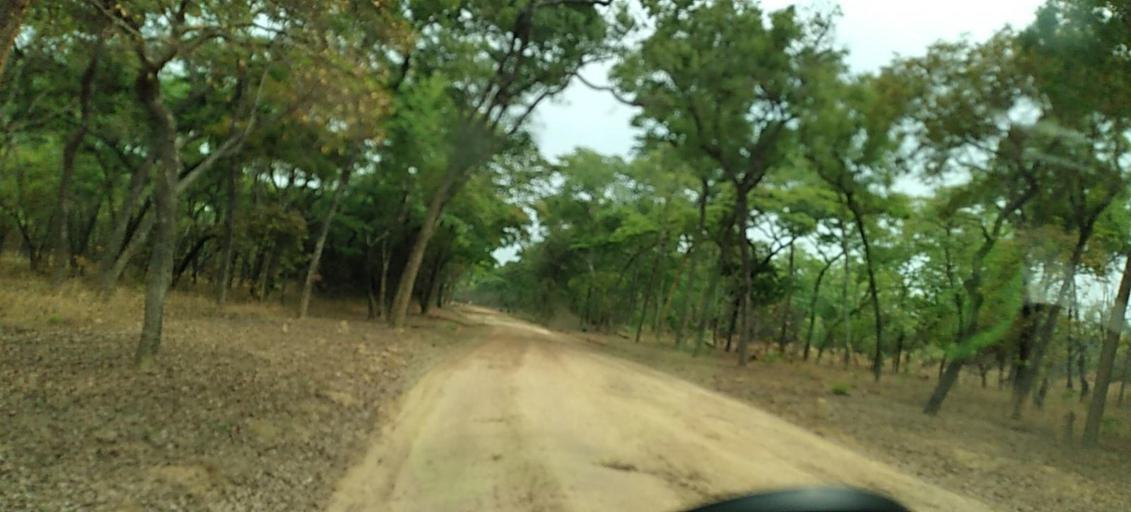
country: ZM
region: North-Western
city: Solwezi
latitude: -12.9462
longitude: 26.5591
